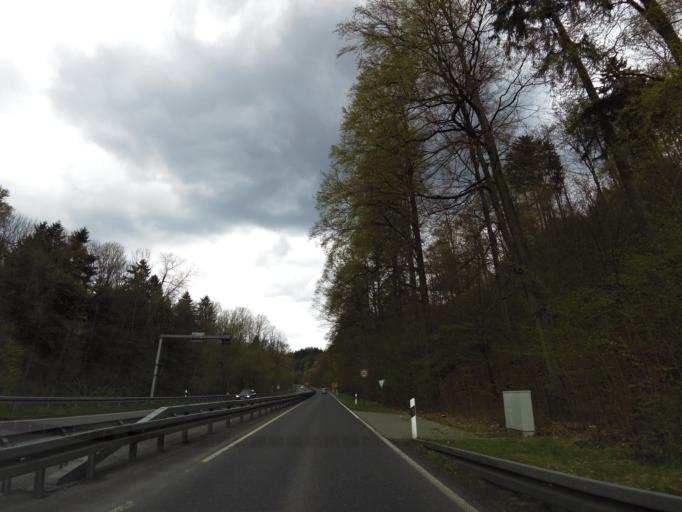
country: DE
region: Lower Saxony
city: Osterode am Harz
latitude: 51.7365
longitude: 10.2727
